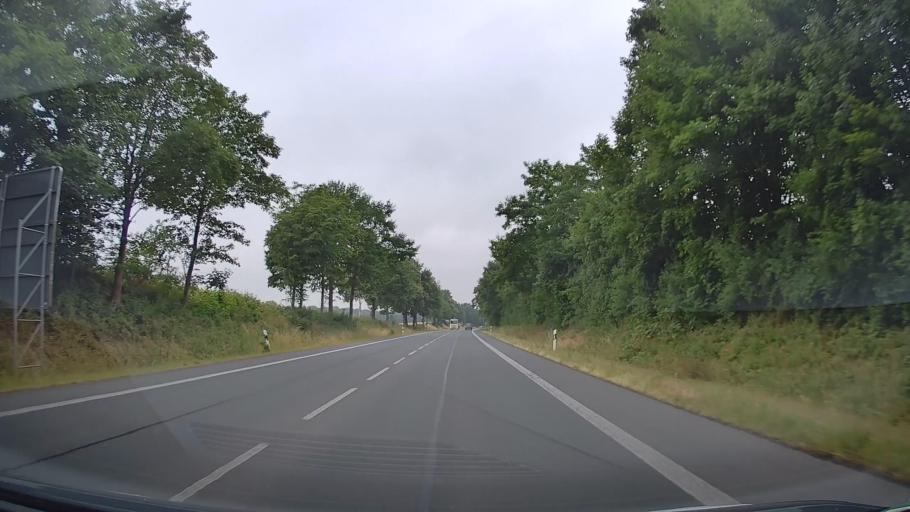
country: DE
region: North Rhine-Westphalia
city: Rahden
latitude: 52.4285
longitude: 8.6027
